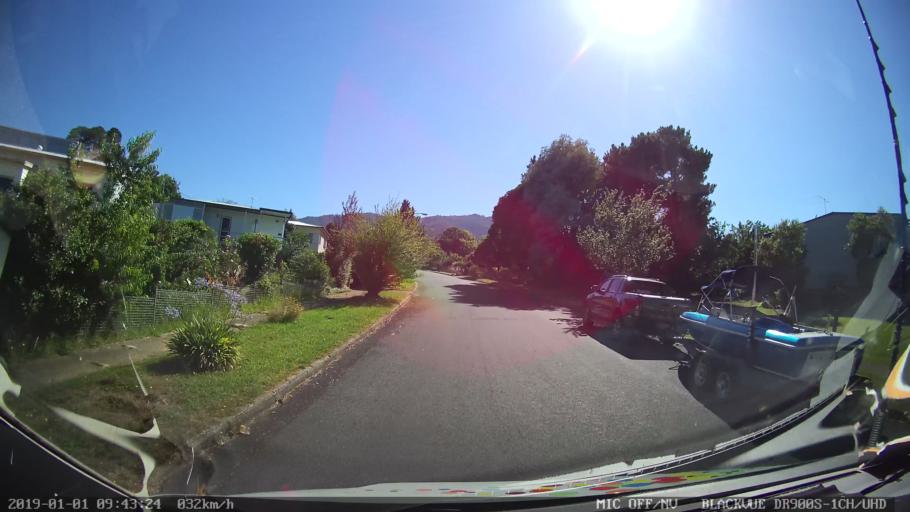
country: AU
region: New South Wales
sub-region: Snowy River
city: Jindabyne
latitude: -36.2152
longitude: 148.1340
